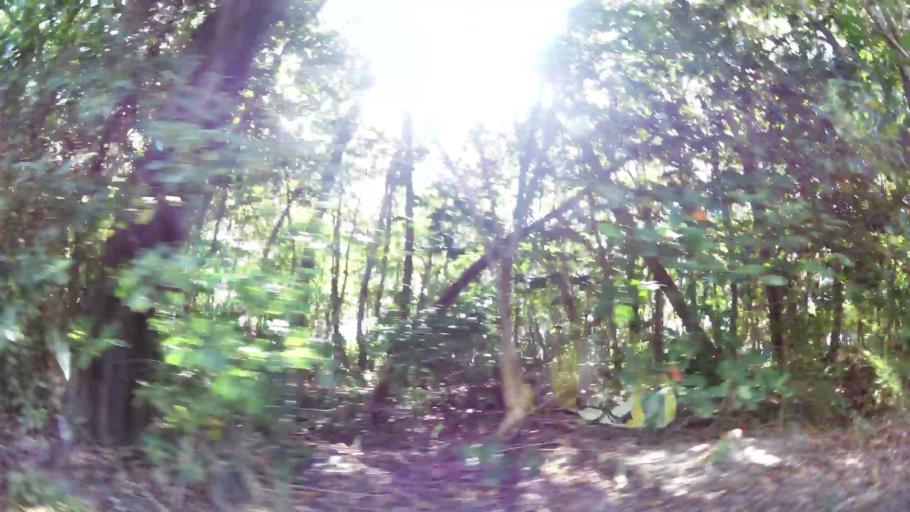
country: MQ
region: Martinique
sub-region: Martinique
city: Les Trois-Ilets
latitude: 14.4752
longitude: -61.0389
